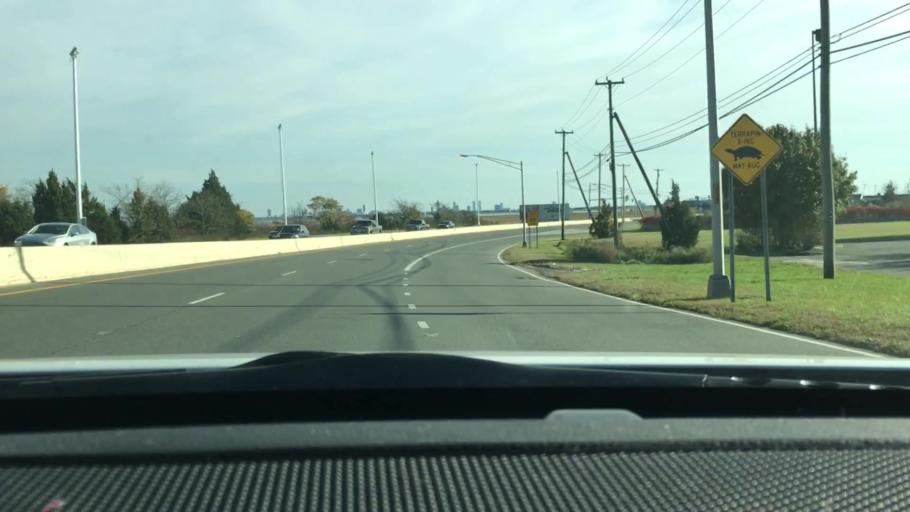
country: US
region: New Jersey
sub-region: Atlantic County
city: Absecon
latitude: 39.4174
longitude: -74.4921
